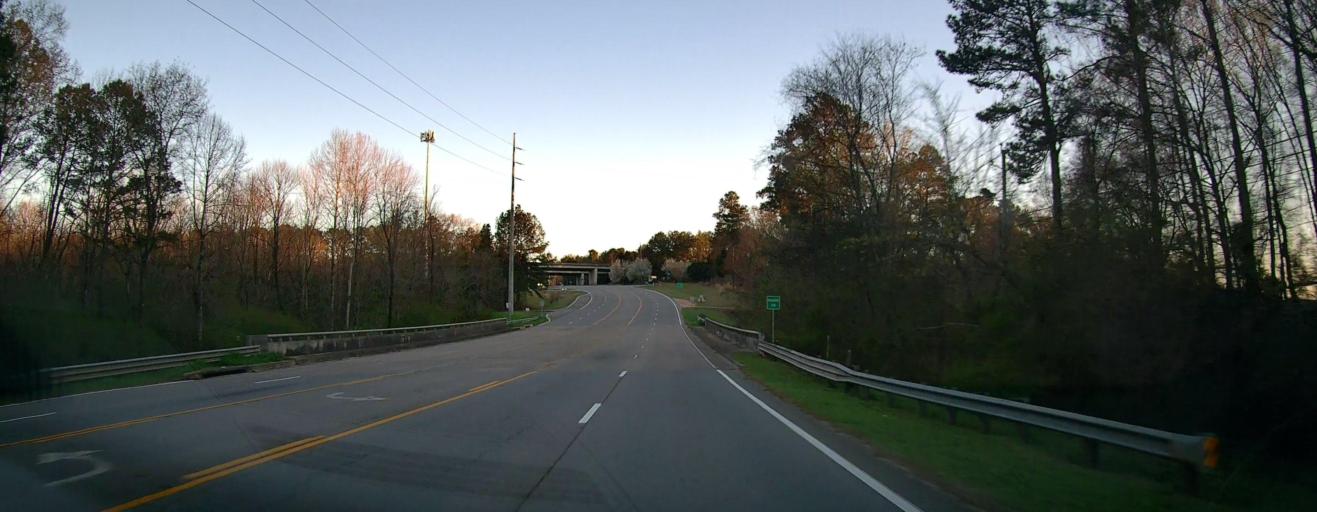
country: US
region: Alabama
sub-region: Russell County
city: Phenix City
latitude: 32.5250
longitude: -84.9909
